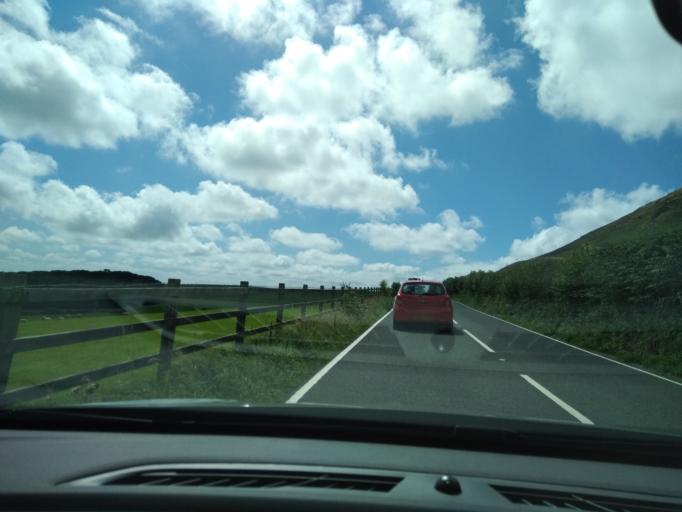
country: GB
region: England
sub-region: Cumbria
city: Millom
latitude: 54.2419
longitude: -3.3174
